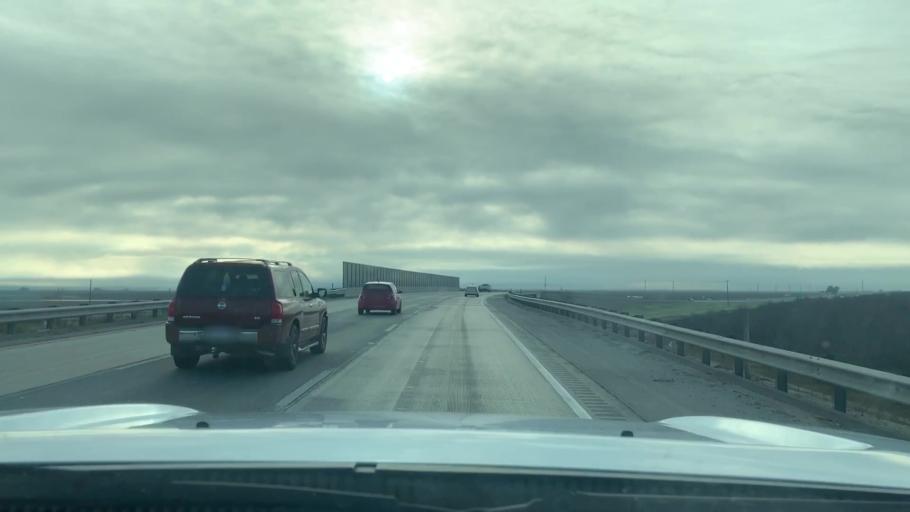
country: US
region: California
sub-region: Kern County
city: McFarland
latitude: 35.5918
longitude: -119.2072
